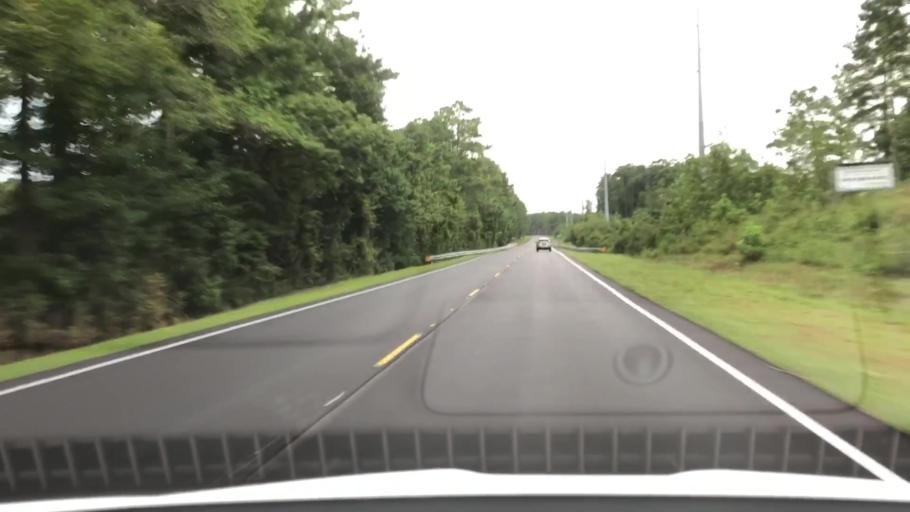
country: US
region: North Carolina
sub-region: Carteret County
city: Cape Carteret
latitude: 34.7647
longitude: -77.0959
